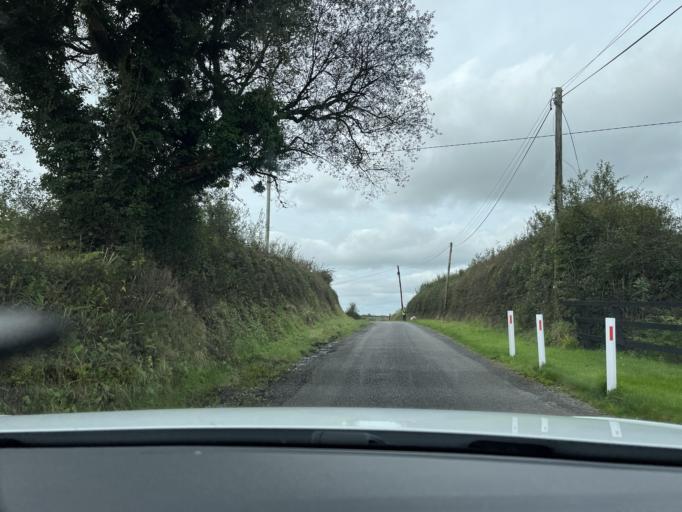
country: IE
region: Connaught
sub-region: County Leitrim
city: Carrick-on-Shannon
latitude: 53.9674
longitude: -8.0978
